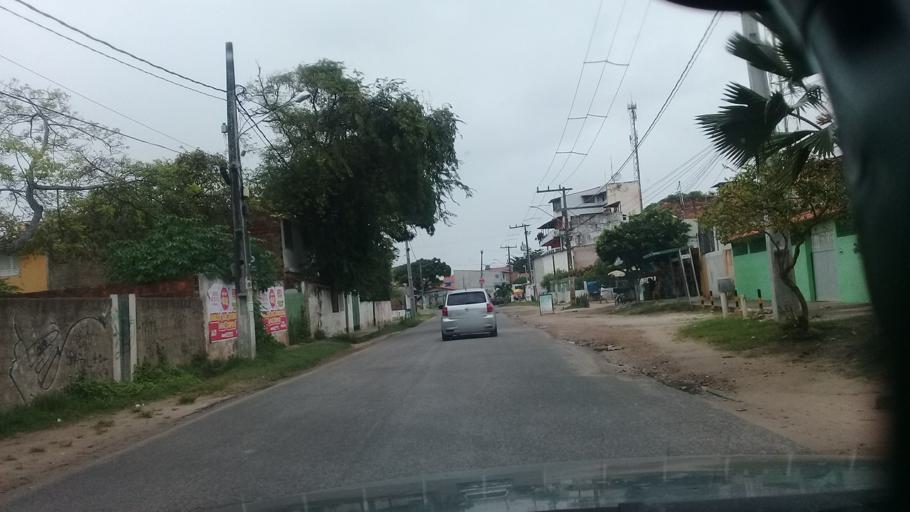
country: BR
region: Pernambuco
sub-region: Itamaraca
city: Itamaraca
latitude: -7.7424
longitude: -34.8245
